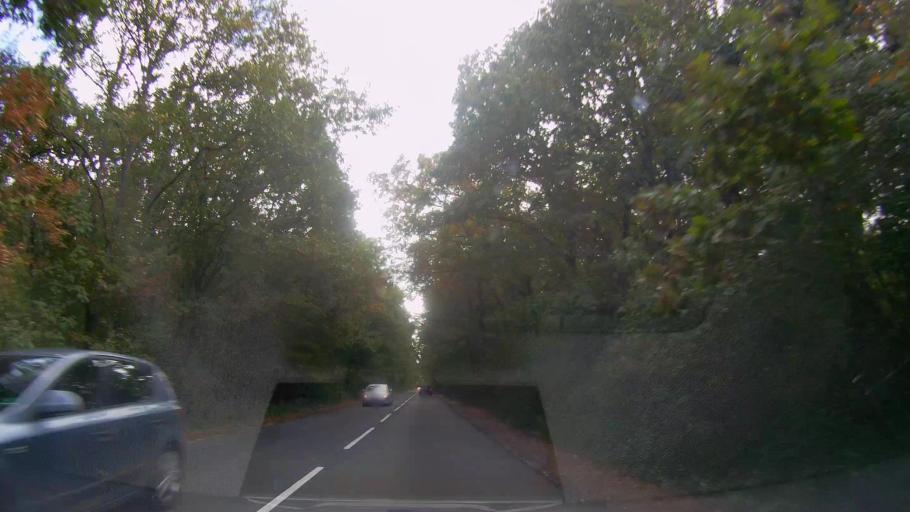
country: BG
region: Burgas
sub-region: Obshtina Primorsko
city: Primorsko
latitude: 42.2985
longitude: 27.7295
